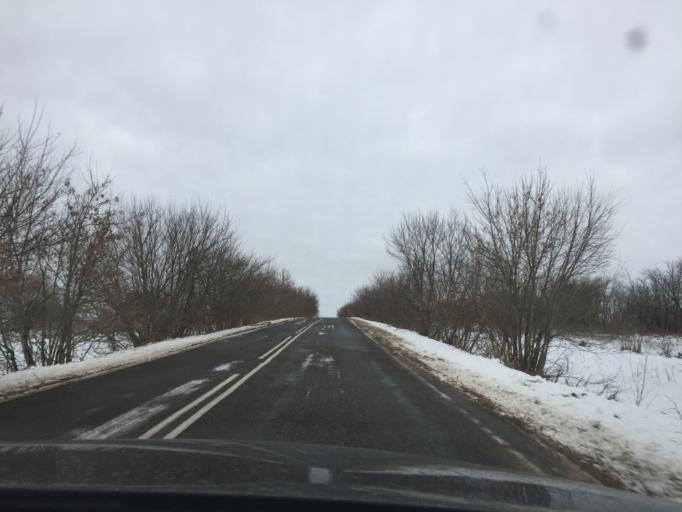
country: RU
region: Tula
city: Teploye
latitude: 53.7872
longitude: 37.6176
